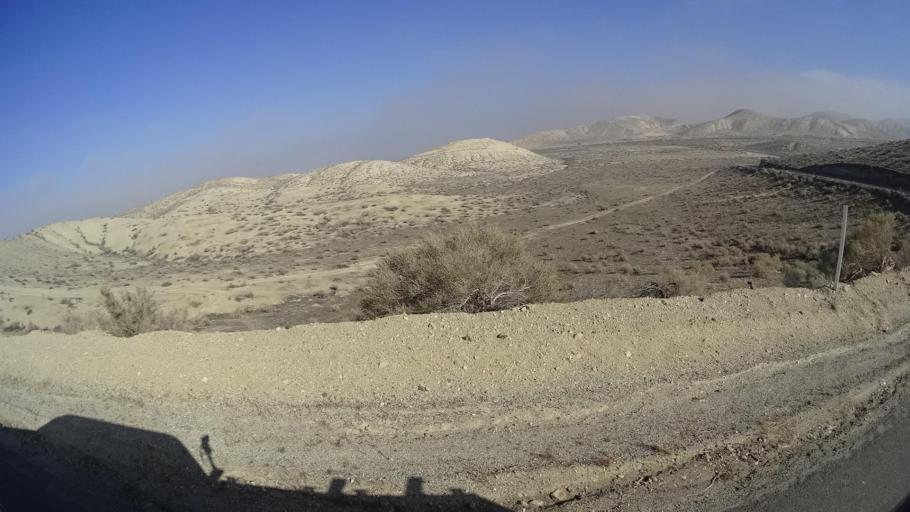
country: US
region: California
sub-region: Kern County
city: Maricopa
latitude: 35.0402
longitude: -119.4282
